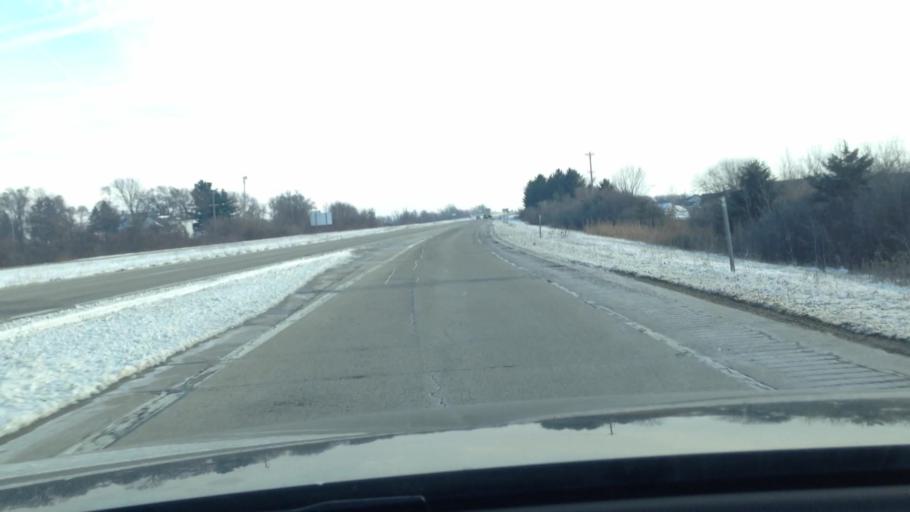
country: US
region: Wisconsin
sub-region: Walworth County
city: Elkhorn
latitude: 42.6644
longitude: -88.5151
